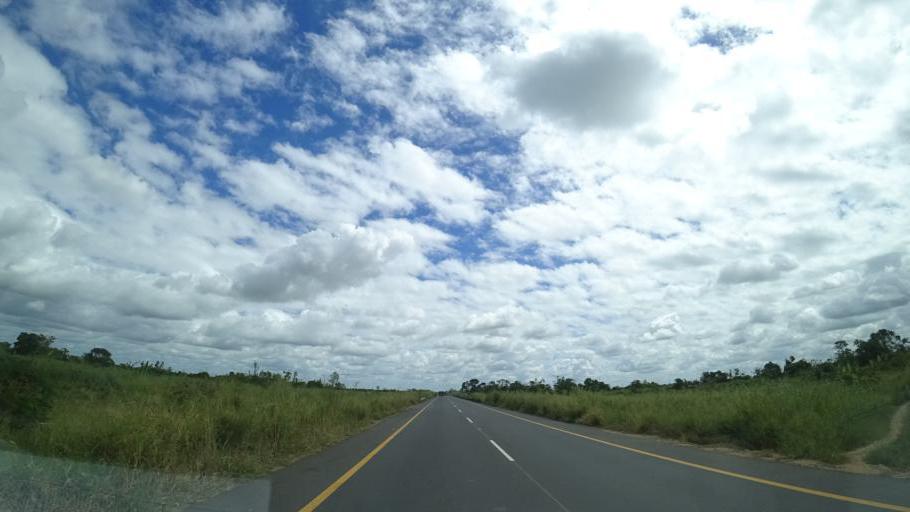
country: MZ
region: Sofala
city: Dondo
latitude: -19.3903
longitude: 34.4169
